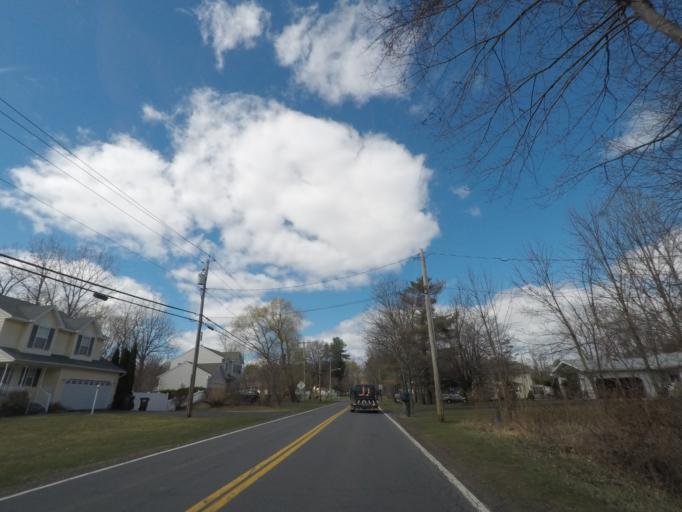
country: US
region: New York
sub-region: Albany County
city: Delmar
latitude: 42.5819
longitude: -73.8295
